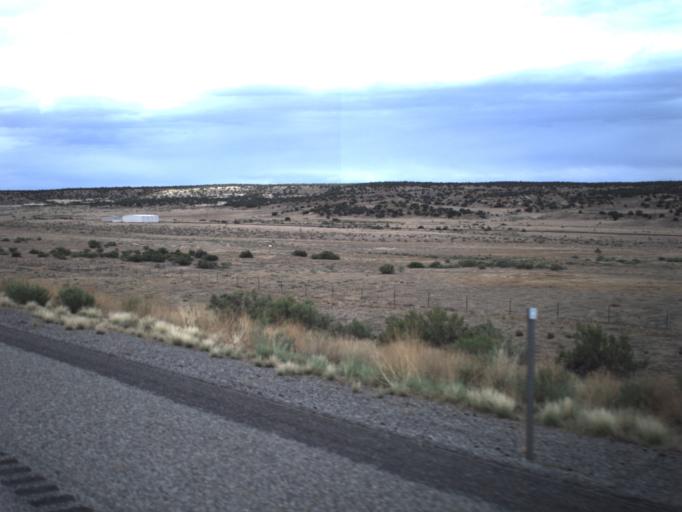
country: US
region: Colorado
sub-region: Mesa County
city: Loma
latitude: 39.1455
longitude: -109.1513
